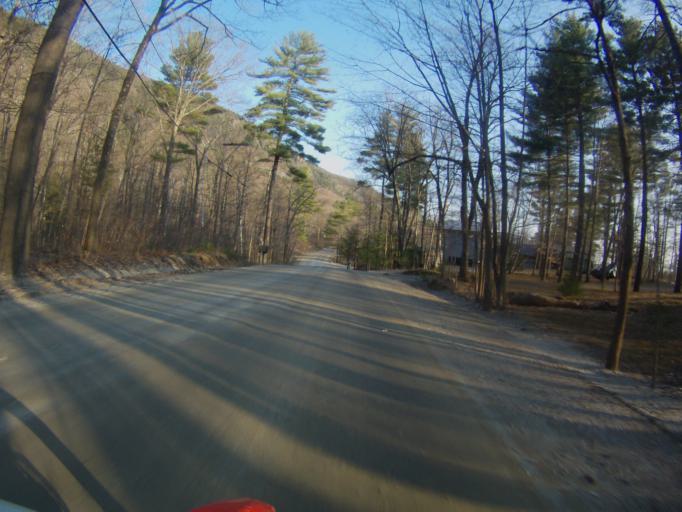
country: US
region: Vermont
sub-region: Addison County
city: Bristol
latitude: 44.1147
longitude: -73.0777
